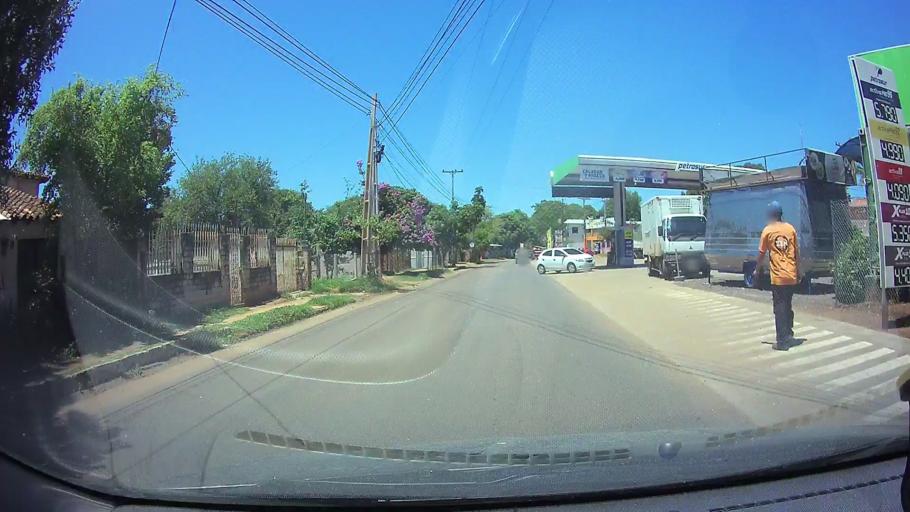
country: PY
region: Central
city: San Lorenzo
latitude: -25.3357
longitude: -57.4853
